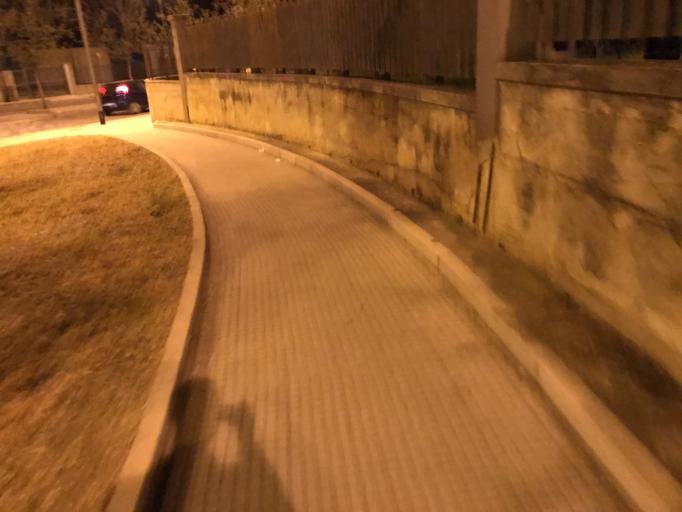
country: IT
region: Apulia
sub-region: Provincia di Bari
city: Corato
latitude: 41.1518
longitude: 16.4019
